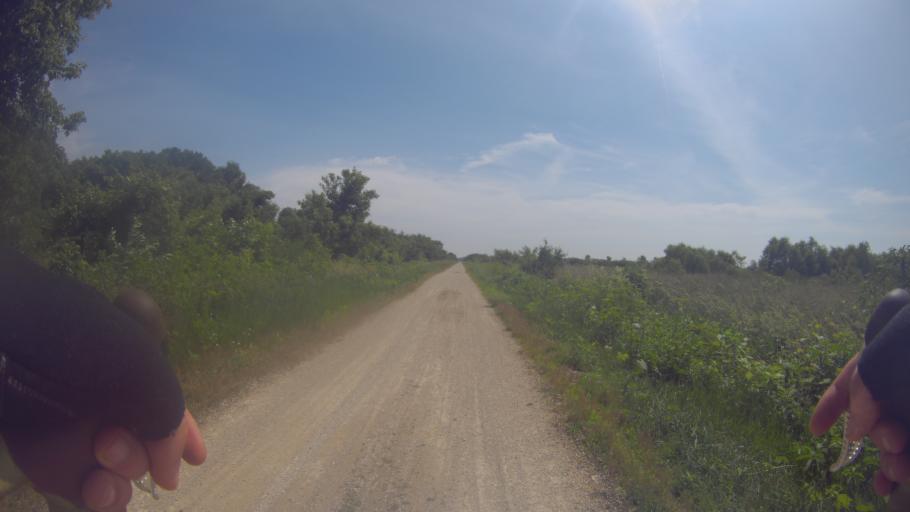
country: US
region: Wisconsin
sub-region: Jefferson County
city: Lake Ripley
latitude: 43.0524
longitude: -88.9964
